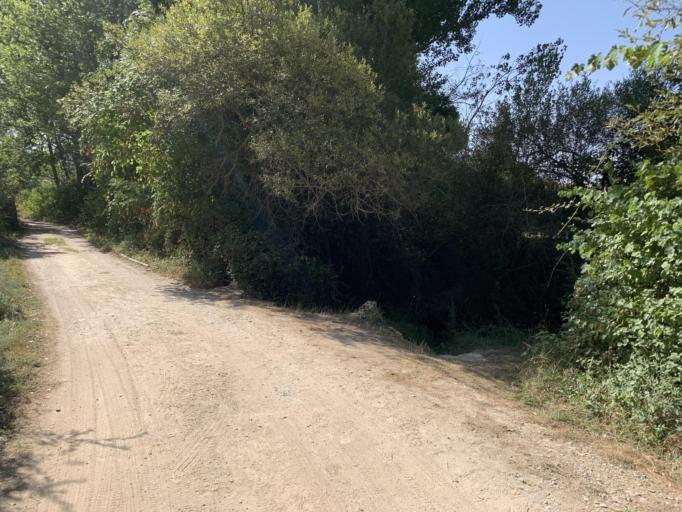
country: ES
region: Castille-La Mancha
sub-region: Provincia de Guadalajara
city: Ocentejo
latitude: 40.7685
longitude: -2.3971
